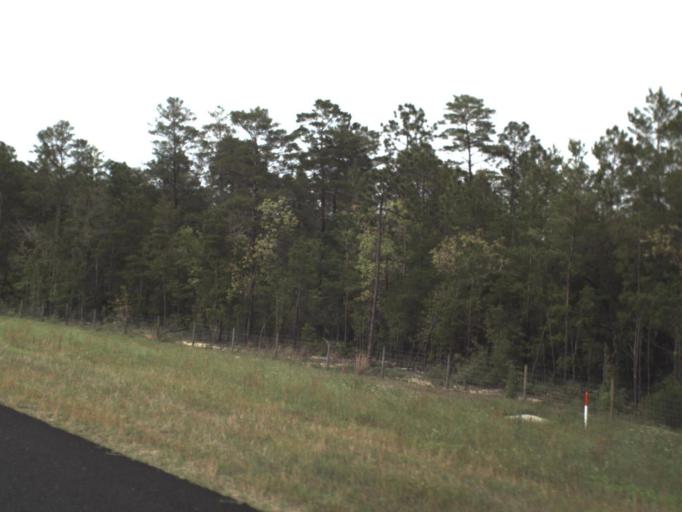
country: US
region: Florida
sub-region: Okaloosa County
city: Niceville
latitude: 30.5302
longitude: -86.4186
